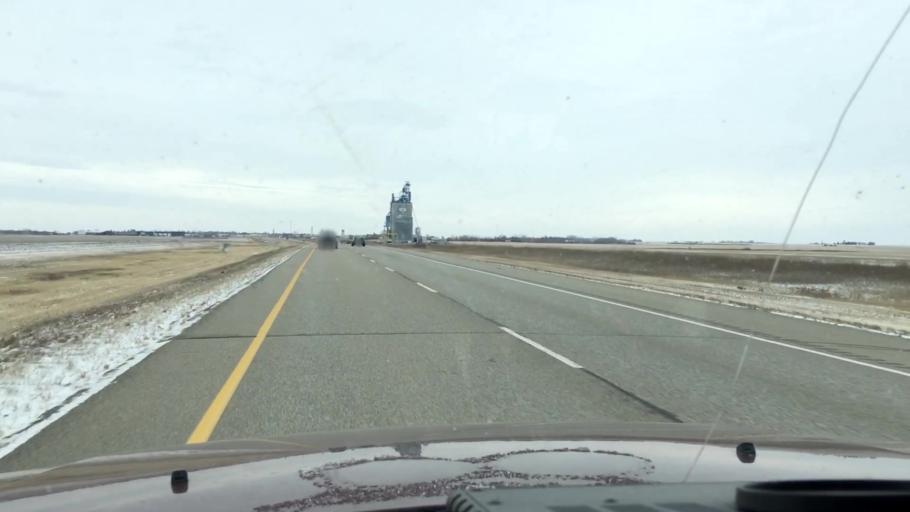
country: CA
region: Saskatchewan
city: Watrous
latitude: 51.2864
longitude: -106.0238
